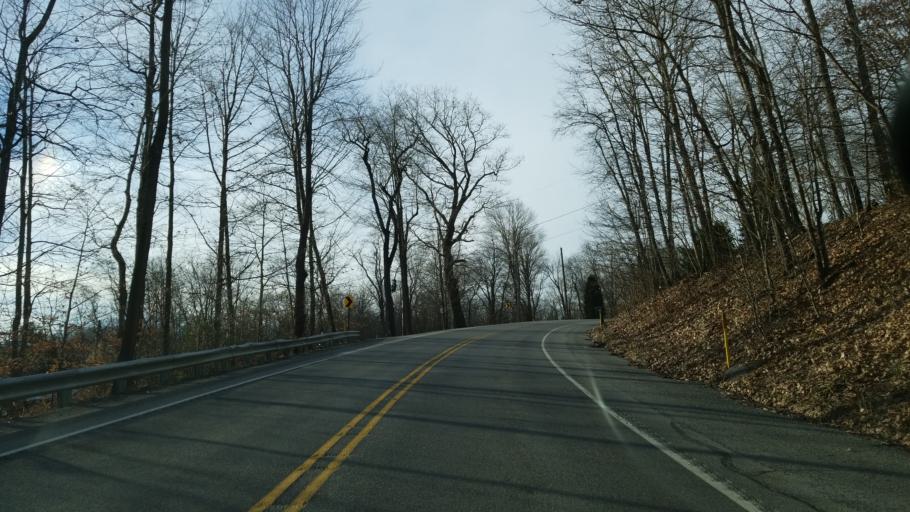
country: US
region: Pennsylvania
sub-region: Clearfield County
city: Curwensville
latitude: 40.9725
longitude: -78.6215
